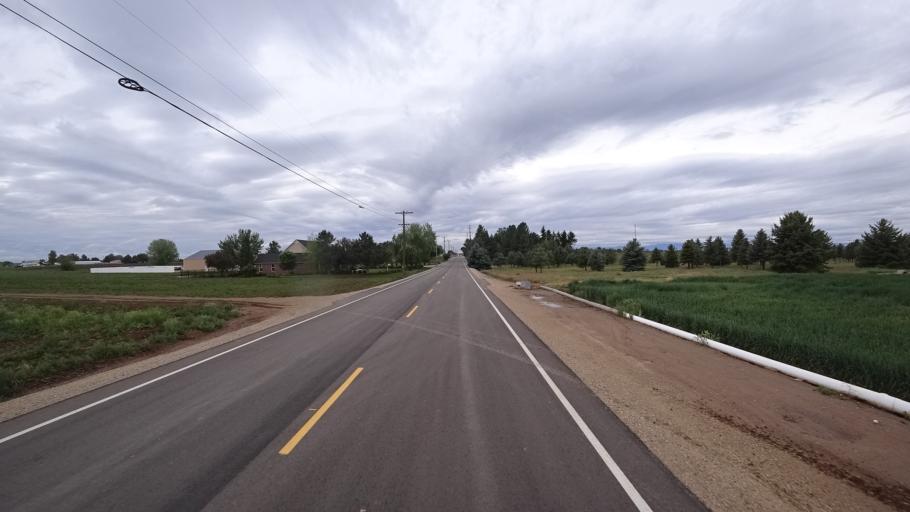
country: US
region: Idaho
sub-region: Ada County
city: Star
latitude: 43.6671
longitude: -116.5129
